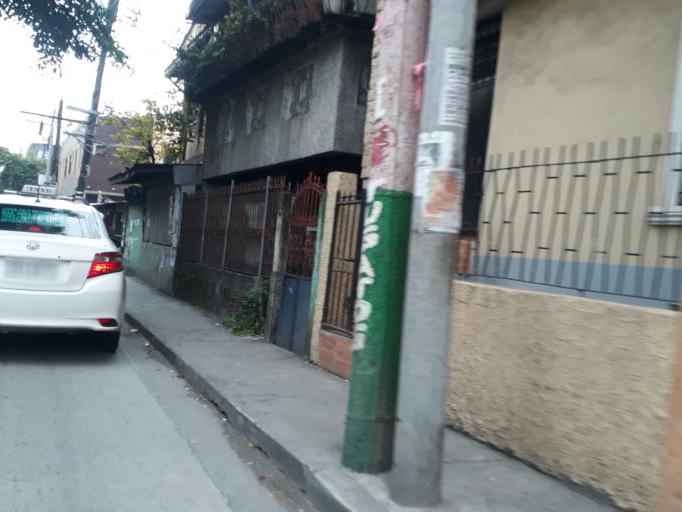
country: PH
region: Metro Manila
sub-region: Caloocan City
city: Niugan
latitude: 14.6618
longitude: 120.9691
